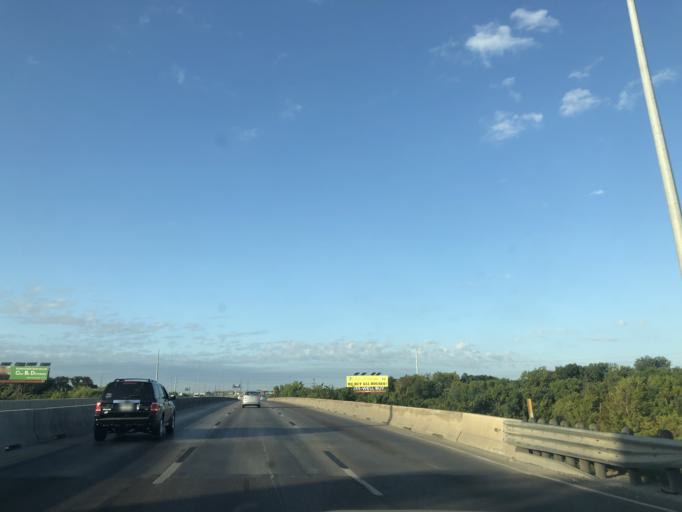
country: US
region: Texas
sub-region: Dallas County
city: Irving
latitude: 32.8563
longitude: -96.9046
